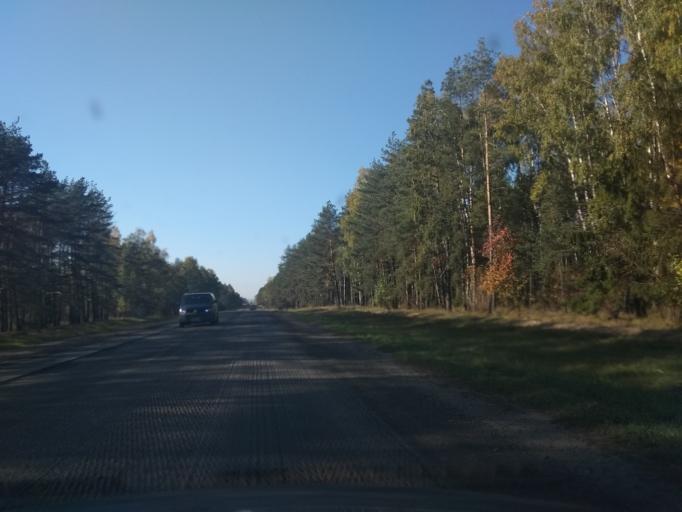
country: BY
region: Grodnenskaya
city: Zhyrovichy
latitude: 53.0595
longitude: 25.4334
